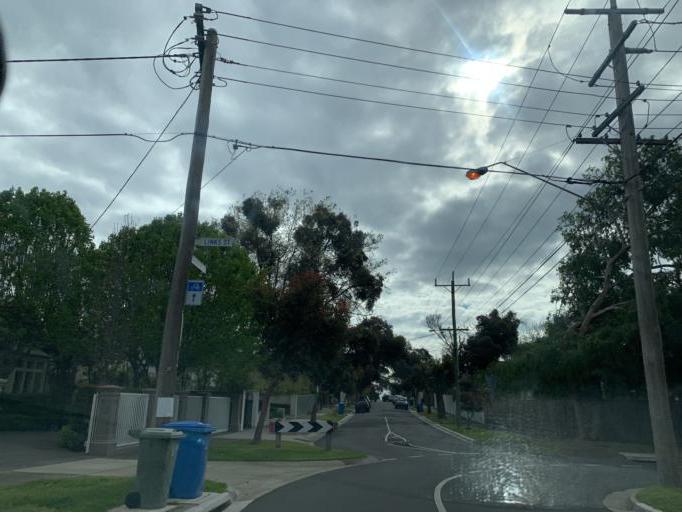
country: AU
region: Victoria
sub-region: Bayside
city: Black Rock
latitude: -37.9719
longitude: 145.0217
